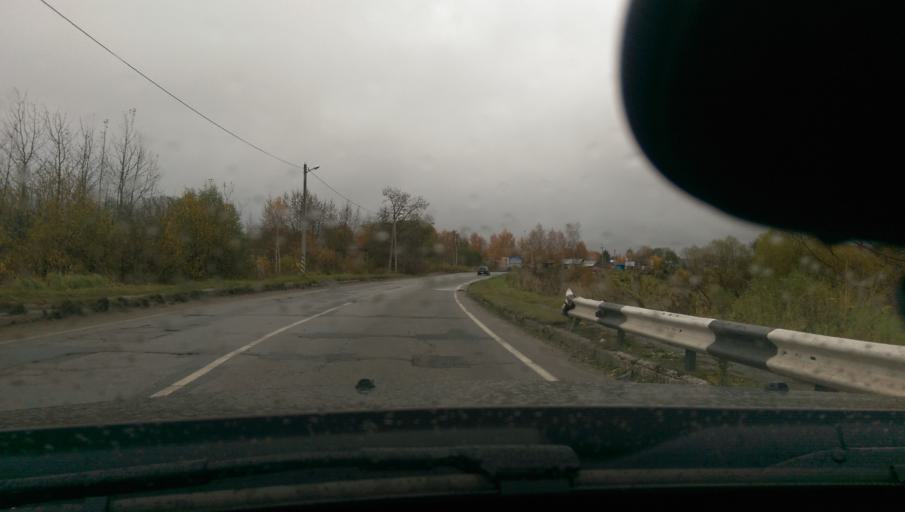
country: RU
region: Jaroslavl
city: Poshekhon'ye
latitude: 58.5105
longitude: 39.1274
